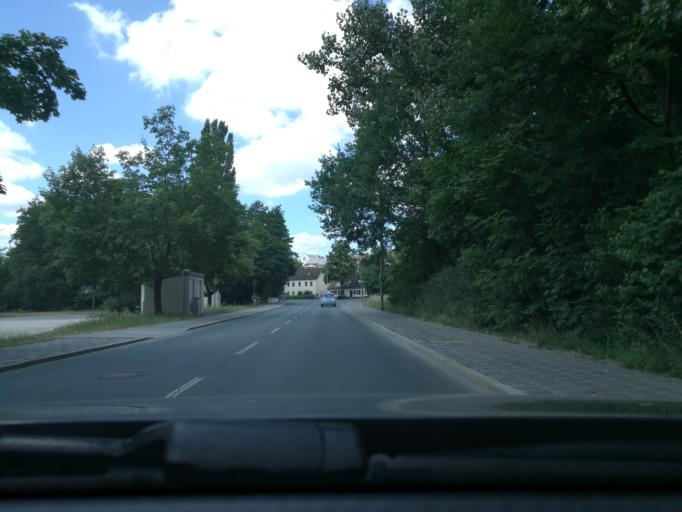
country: DE
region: Bavaria
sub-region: Regierungsbezirk Mittelfranken
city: Furth
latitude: 49.4907
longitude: 10.9563
